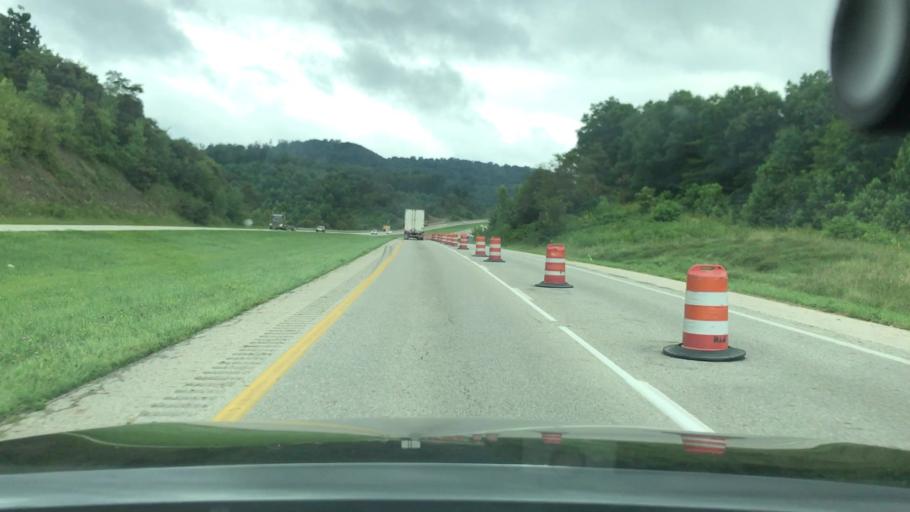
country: US
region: Ohio
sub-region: Ross County
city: Chillicothe
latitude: 39.2438
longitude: -82.8442
